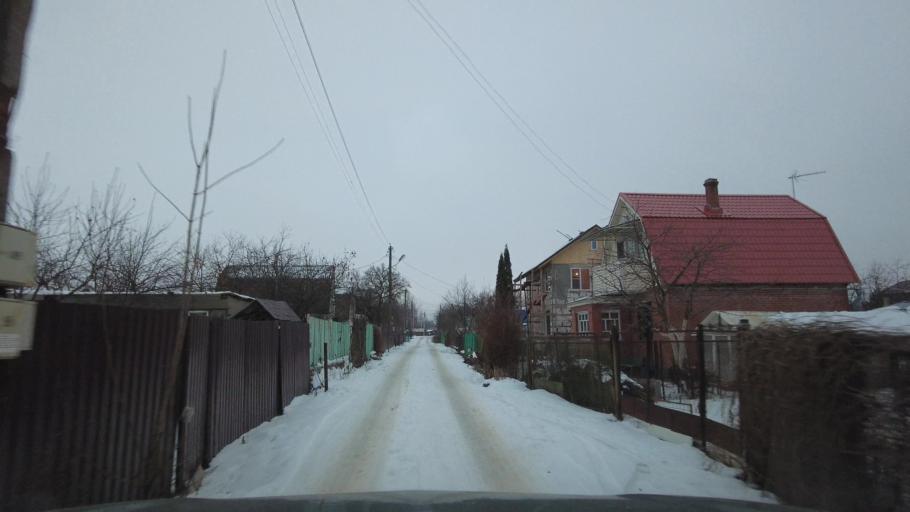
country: RU
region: Moskovskaya
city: Novopodrezkovo
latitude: 55.9850
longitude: 37.3919
